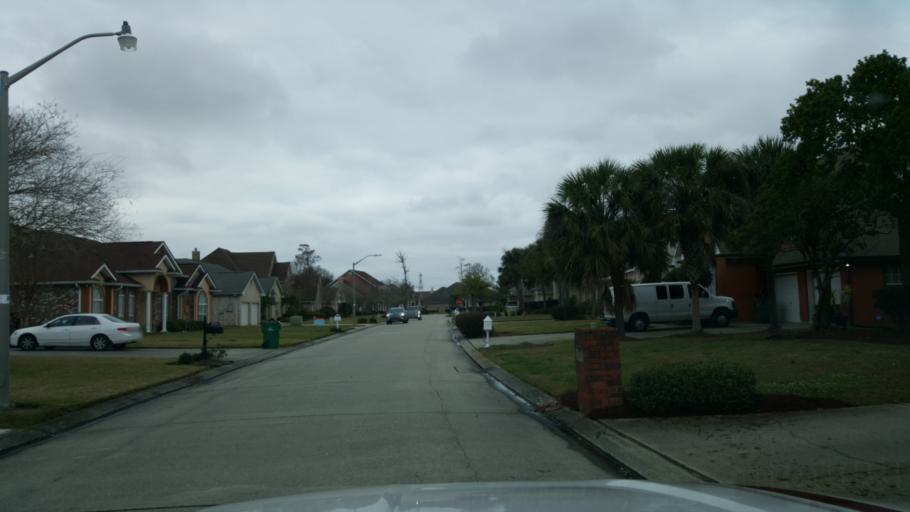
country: US
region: Louisiana
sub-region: Jefferson Parish
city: Woodmere
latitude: 29.8746
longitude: -90.0808
